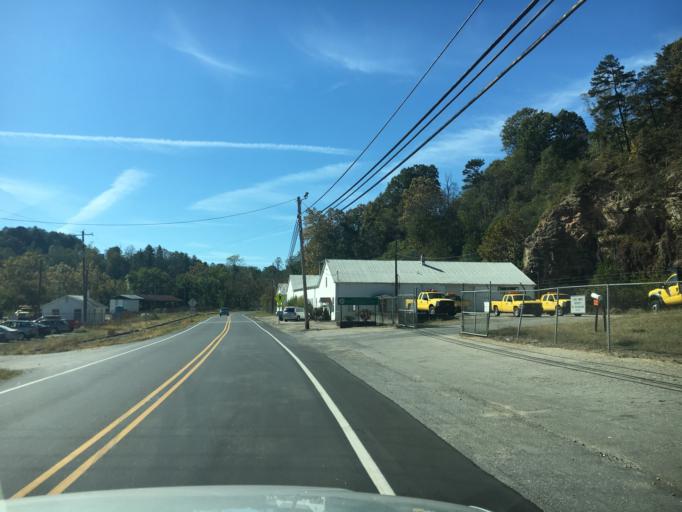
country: US
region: North Carolina
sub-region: Buncombe County
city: Woodfin
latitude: 35.6241
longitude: -82.5948
